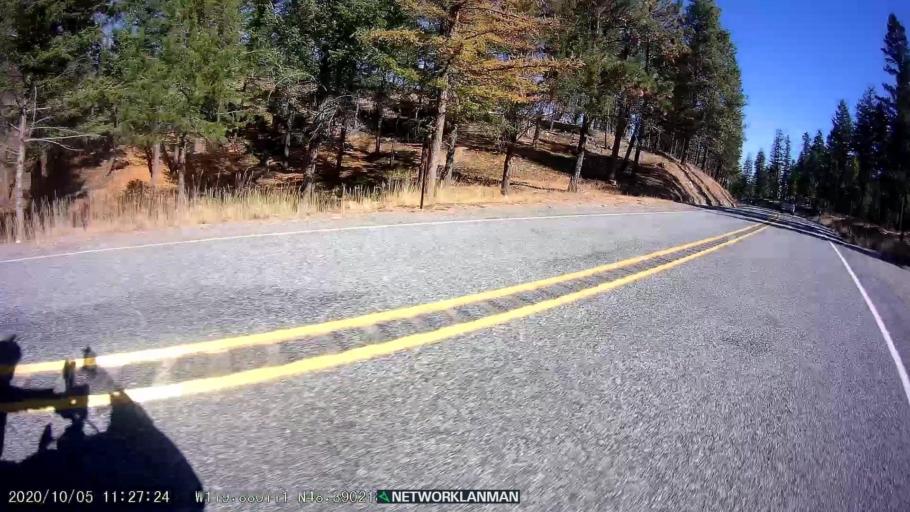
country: US
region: Washington
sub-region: Okanogan County
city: Okanogan
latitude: 48.3903
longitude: -119.8796
